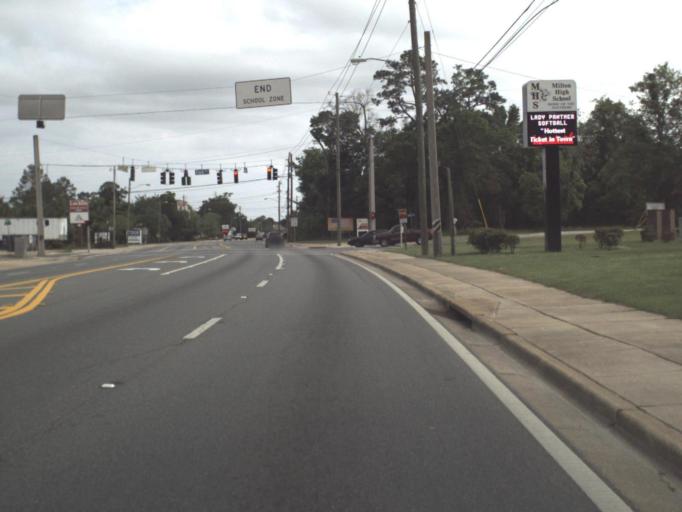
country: US
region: Florida
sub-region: Santa Rosa County
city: Milton
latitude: 30.6315
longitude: -87.0433
